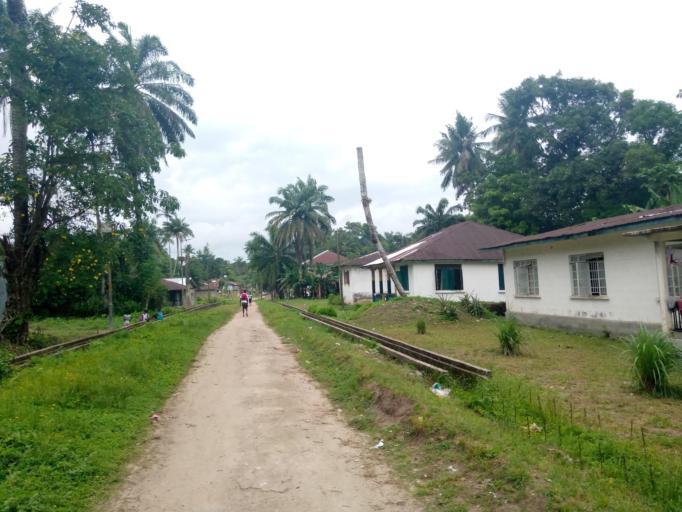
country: SL
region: Southern Province
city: Bonthe
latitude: 7.5246
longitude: -12.5027
